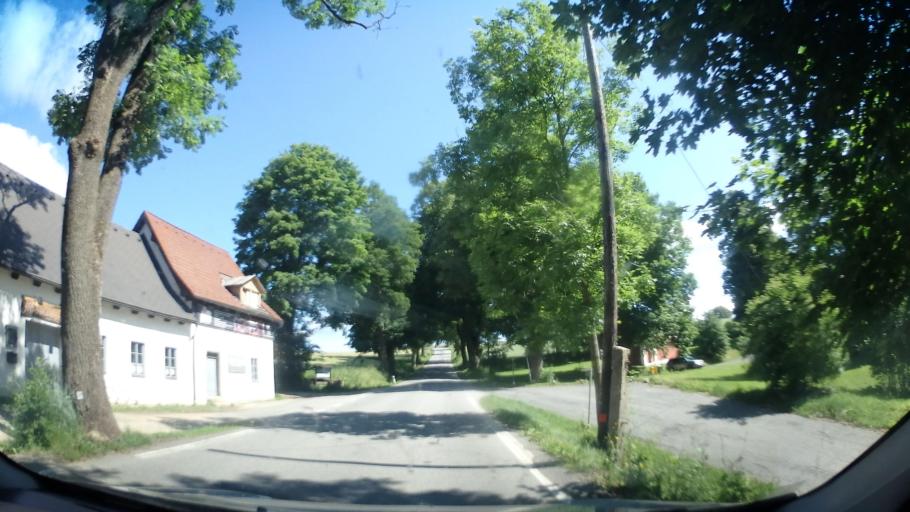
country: CZ
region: Vysocina
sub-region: Okres Zd'ar nad Sazavou
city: Nove Mesto na Morave
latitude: 49.6344
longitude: 16.1179
